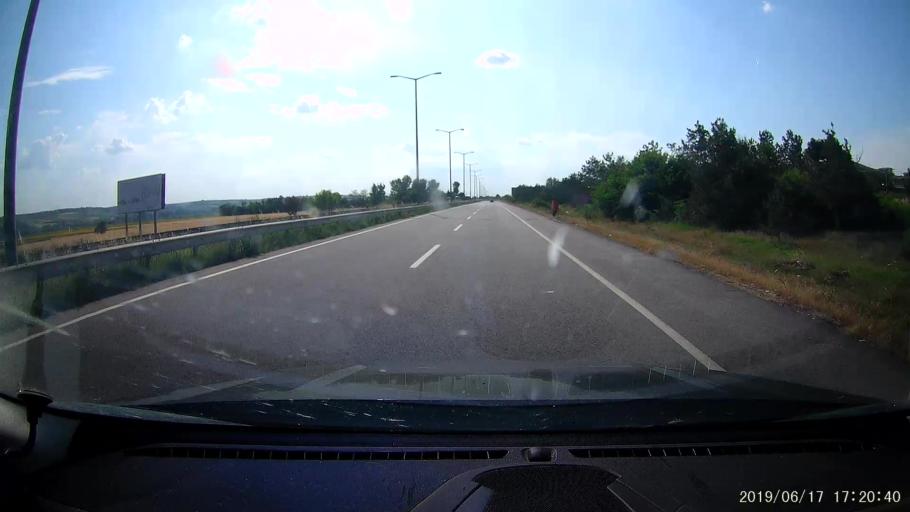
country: GR
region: East Macedonia and Thrace
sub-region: Nomos Evrou
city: Rizia
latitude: 41.7026
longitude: 26.4101
